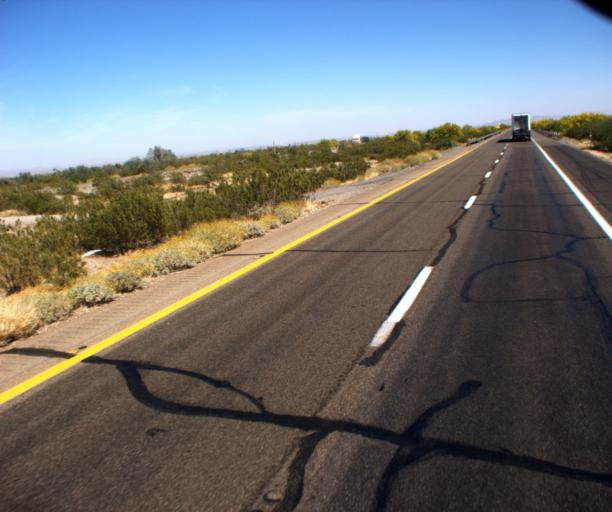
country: US
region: Arizona
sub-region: Pinal County
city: Maricopa
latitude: 32.8298
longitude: -112.0175
